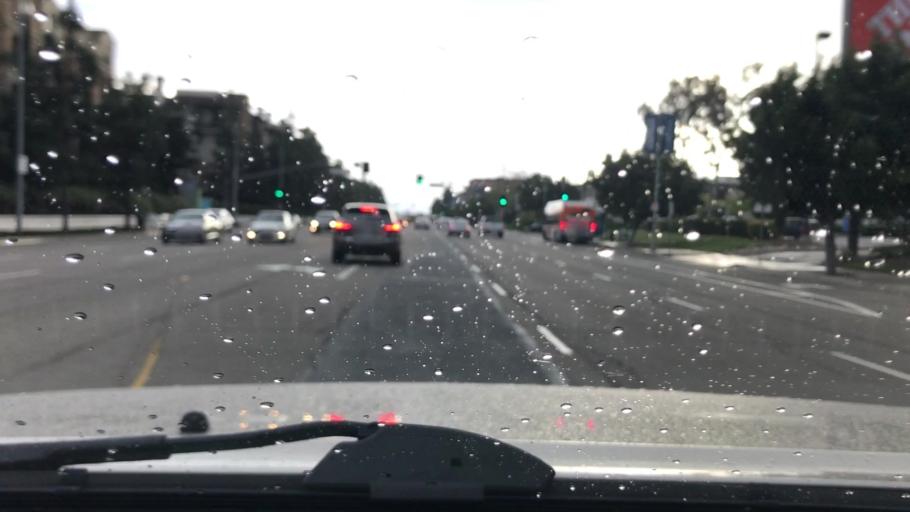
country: US
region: California
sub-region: Los Angeles County
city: Marina del Rey
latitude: 33.9751
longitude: -118.4234
